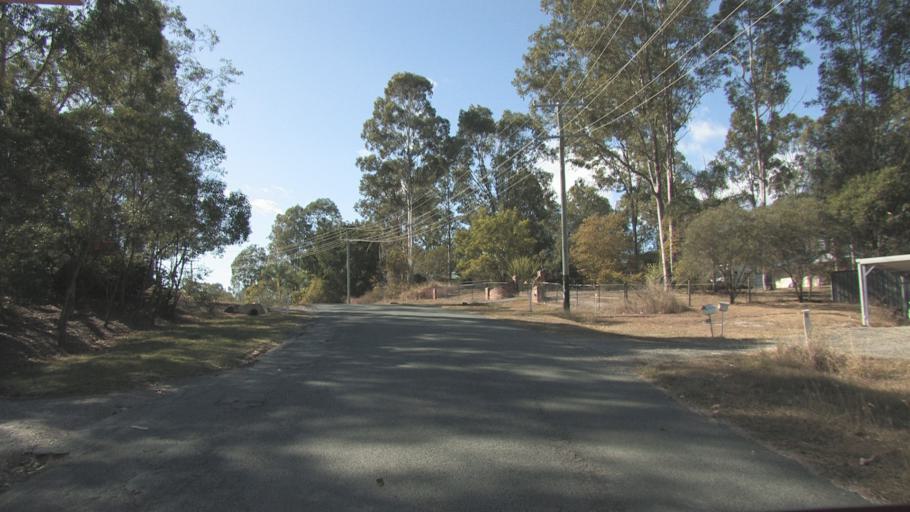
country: AU
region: Queensland
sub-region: Logan
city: Cedar Vale
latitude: -27.8523
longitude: 152.9902
